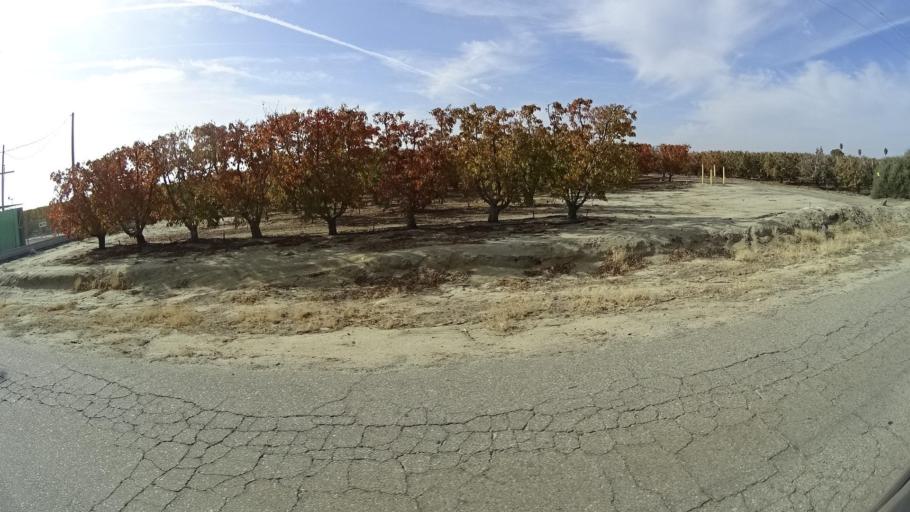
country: US
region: California
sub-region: Kern County
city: Arvin
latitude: 35.2745
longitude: -118.7527
